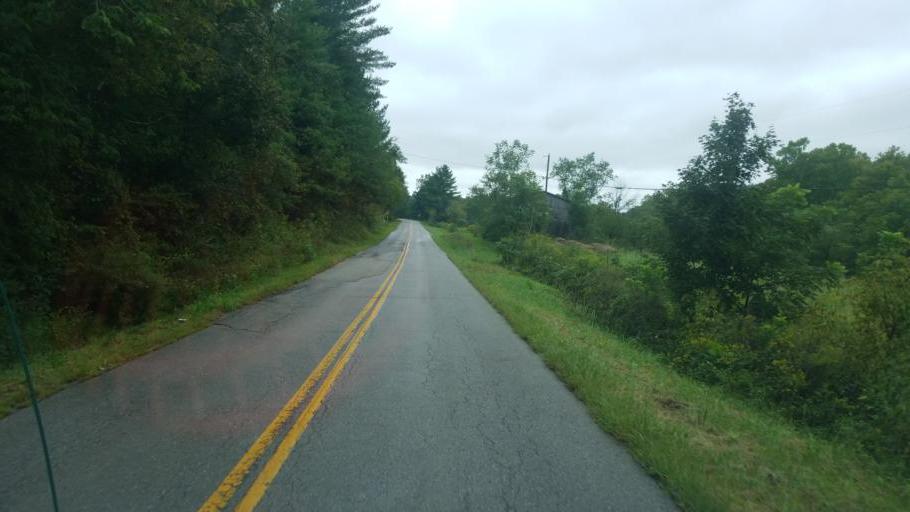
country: US
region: Kentucky
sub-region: Rowan County
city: Morehead
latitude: 38.3628
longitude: -83.5348
